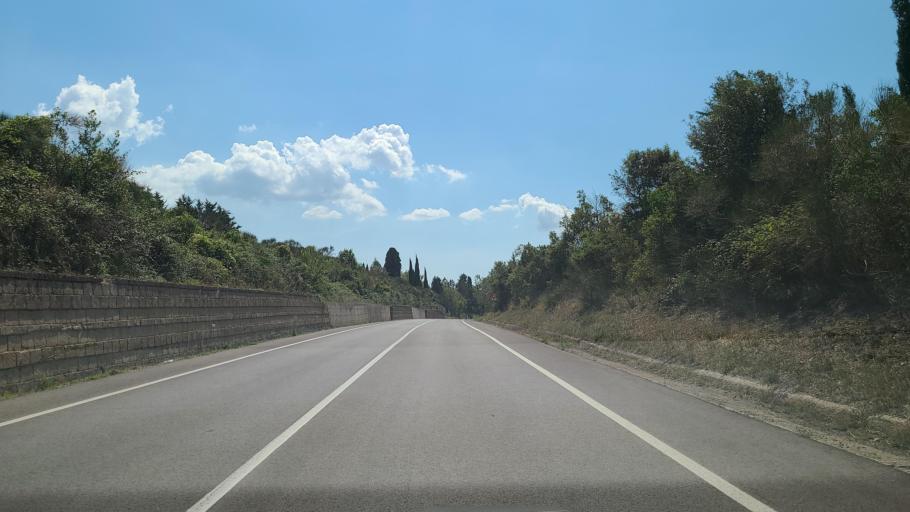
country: IT
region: Tuscany
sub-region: Province of Pisa
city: Volterra
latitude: 43.3932
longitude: 10.9546
